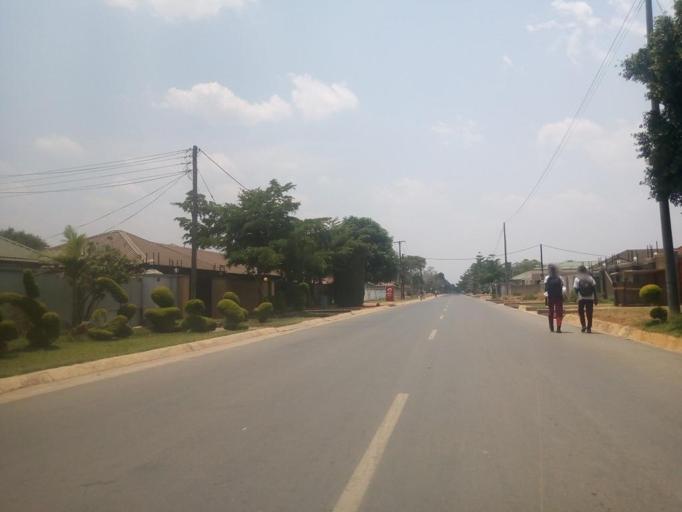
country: ZM
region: Lusaka
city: Lusaka
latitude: -15.3964
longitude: 28.3906
